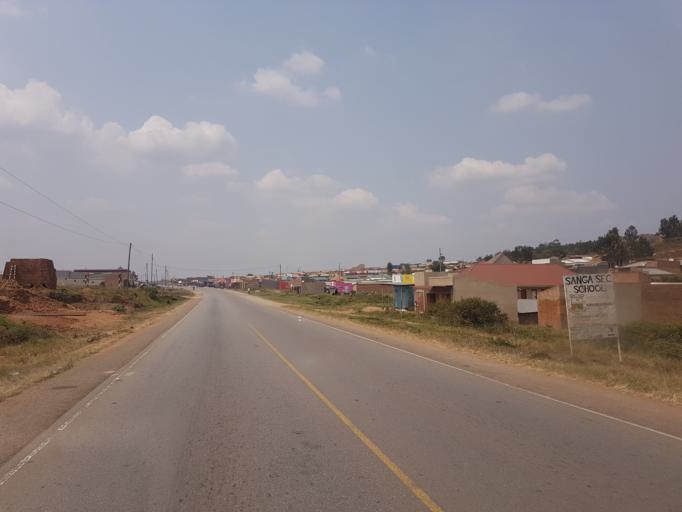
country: UG
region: Central Region
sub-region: Lyantonde District
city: Lyantonde
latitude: -0.5000
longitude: 30.9031
